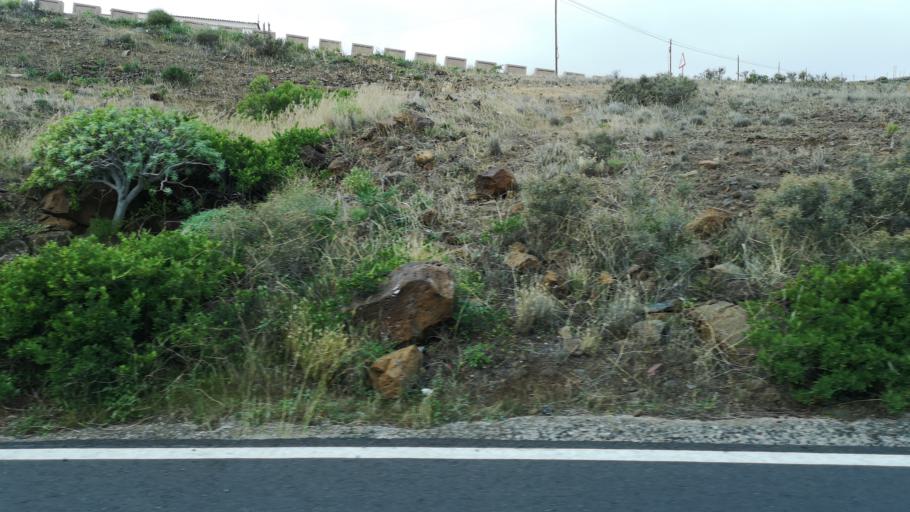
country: ES
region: Canary Islands
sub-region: Provincia de Santa Cruz de Tenerife
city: San Sebastian de la Gomera
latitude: 28.0854
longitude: -17.1372
